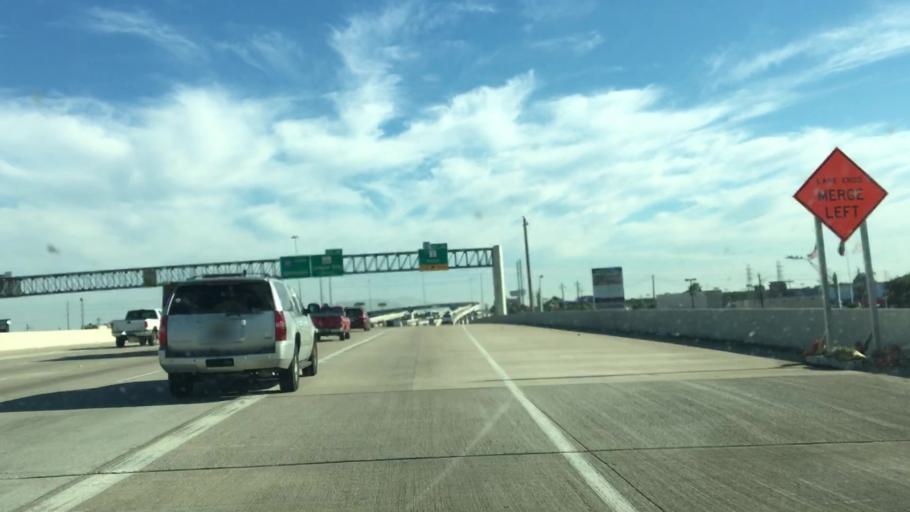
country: US
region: Texas
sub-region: Harris County
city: Webster
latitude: 29.5288
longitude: -95.1313
